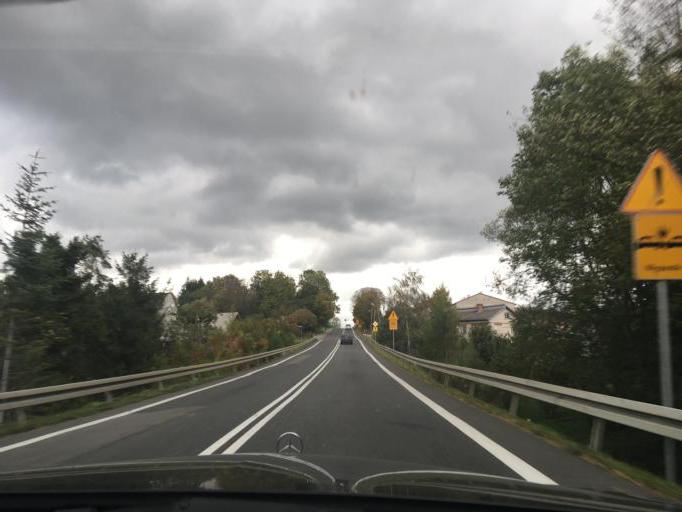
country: PL
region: Subcarpathian Voivodeship
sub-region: Powiat krosnienski
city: Miejsce Piastowe
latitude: 49.6446
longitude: 21.8072
